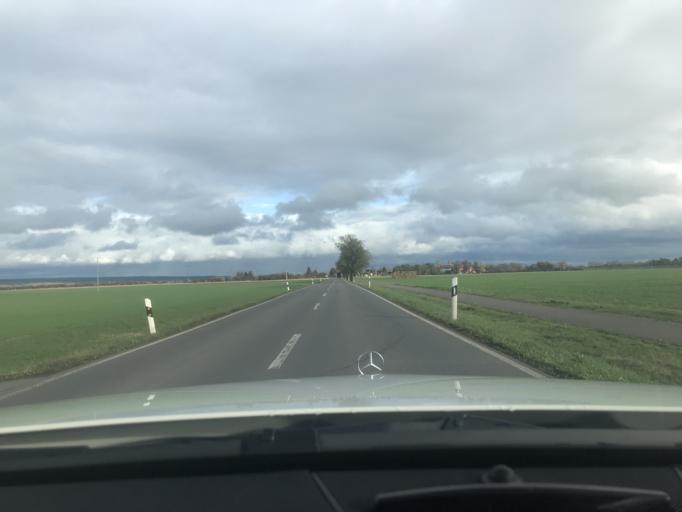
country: DE
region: Thuringia
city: Warza
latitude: 50.9988
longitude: 10.6969
